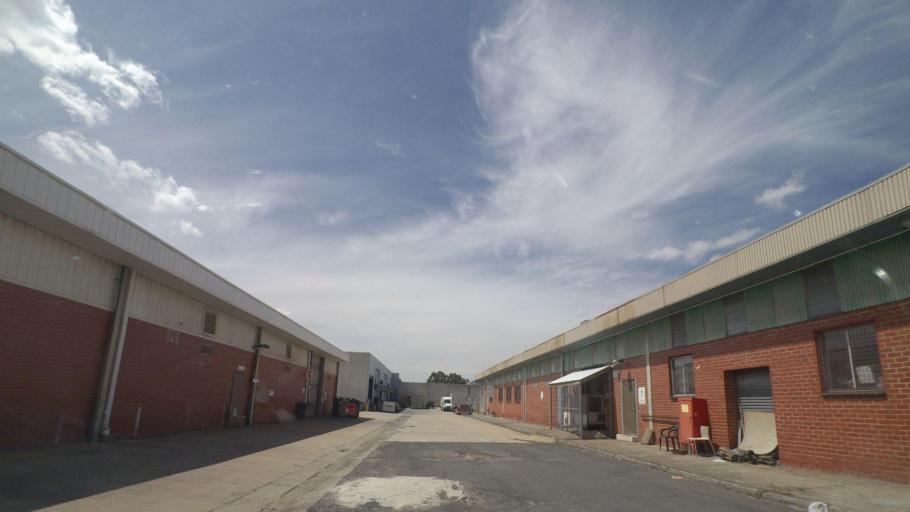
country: AU
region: Victoria
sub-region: Maroondah
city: Bayswater North
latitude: -37.8366
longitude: 145.2931
